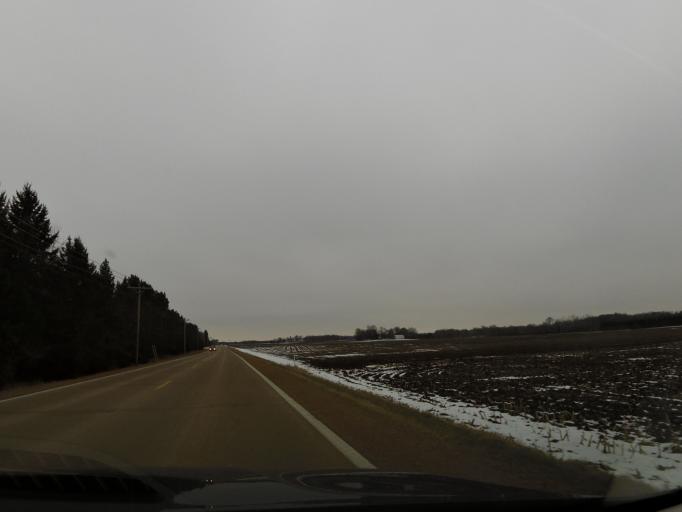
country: US
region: Minnesota
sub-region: Carver County
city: Carver
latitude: 44.7332
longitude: -93.6843
